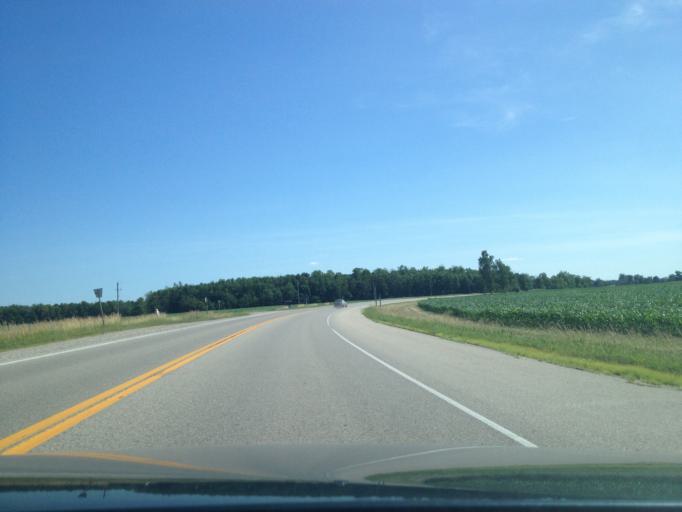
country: CA
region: Ontario
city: Stratford
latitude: 43.4999
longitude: -80.8799
